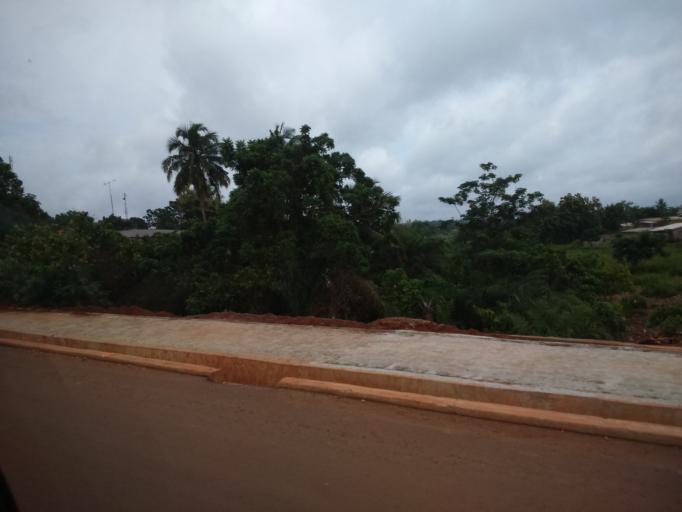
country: CI
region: Moyen-Comoe
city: Abengourou
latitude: 6.7227
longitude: -3.5106
